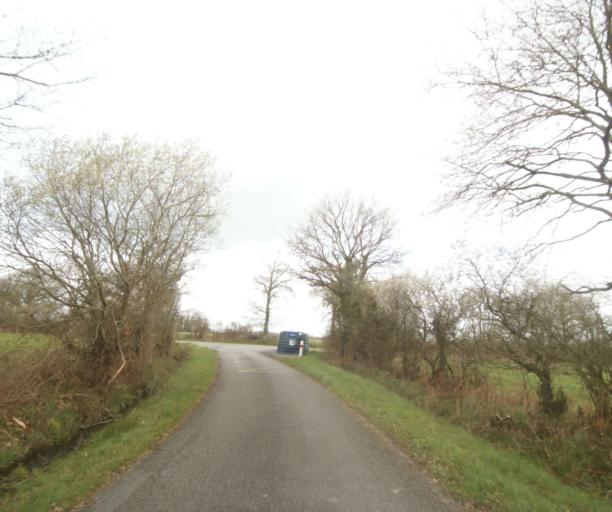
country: FR
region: Pays de la Loire
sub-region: Departement de la Loire-Atlantique
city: Bouvron
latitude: 47.4066
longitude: -1.8796
